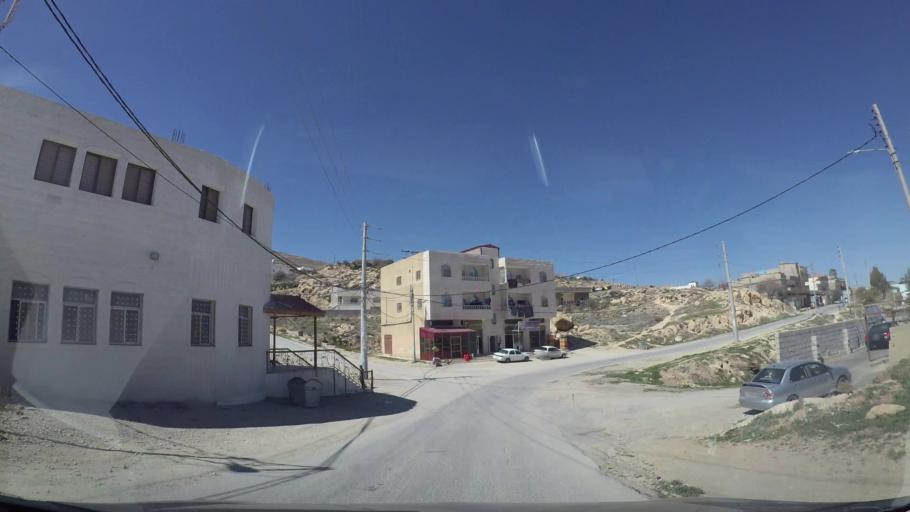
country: JO
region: Tafielah
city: At Tafilah
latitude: 30.8210
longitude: 35.5821
